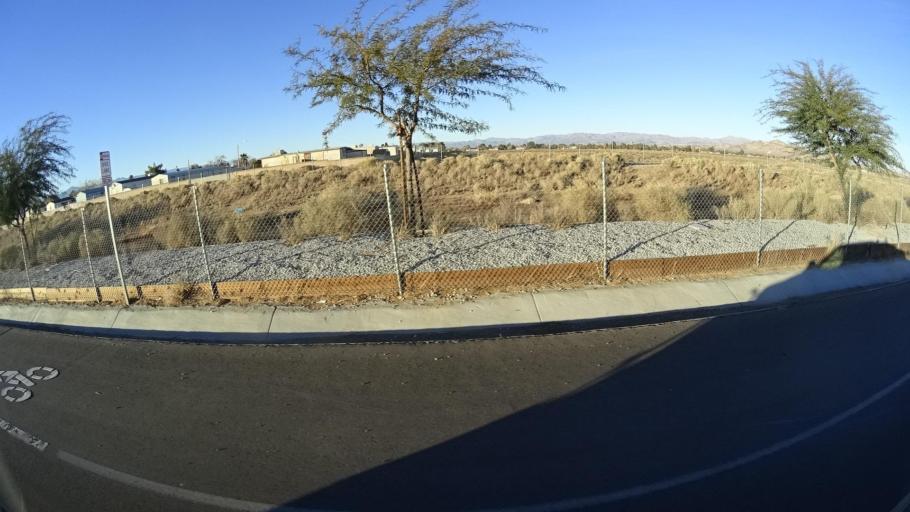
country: US
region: California
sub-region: Kern County
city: Ridgecrest
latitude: 35.6080
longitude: -117.6633
